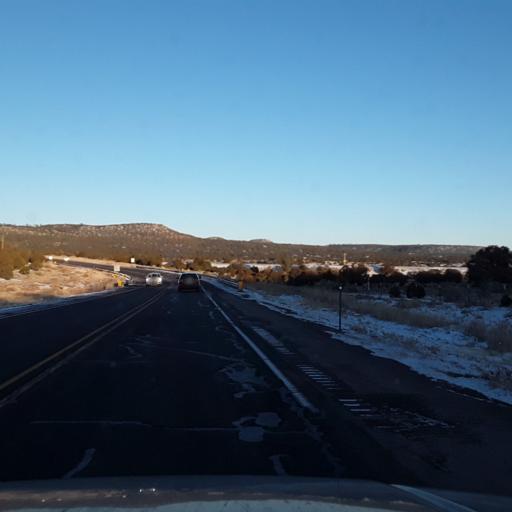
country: US
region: New Mexico
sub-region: Lincoln County
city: Carrizozo
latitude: 34.2394
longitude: -105.6012
